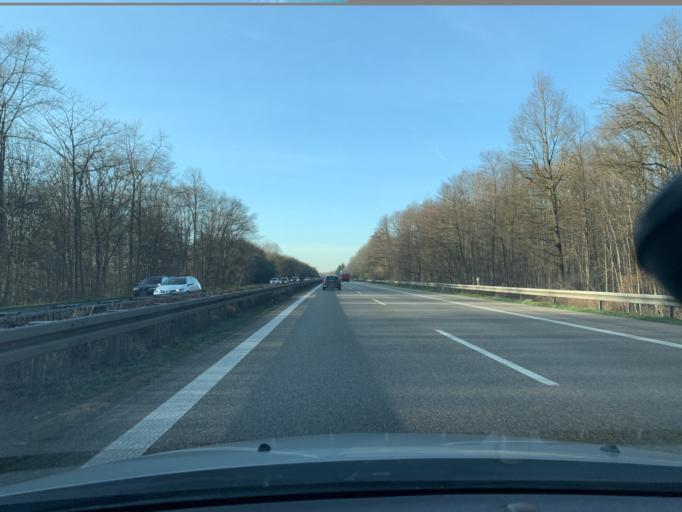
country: DE
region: Baden-Wuerttemberg
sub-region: Freiburg Region
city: Teningen
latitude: 48.1014
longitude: 7.7921
